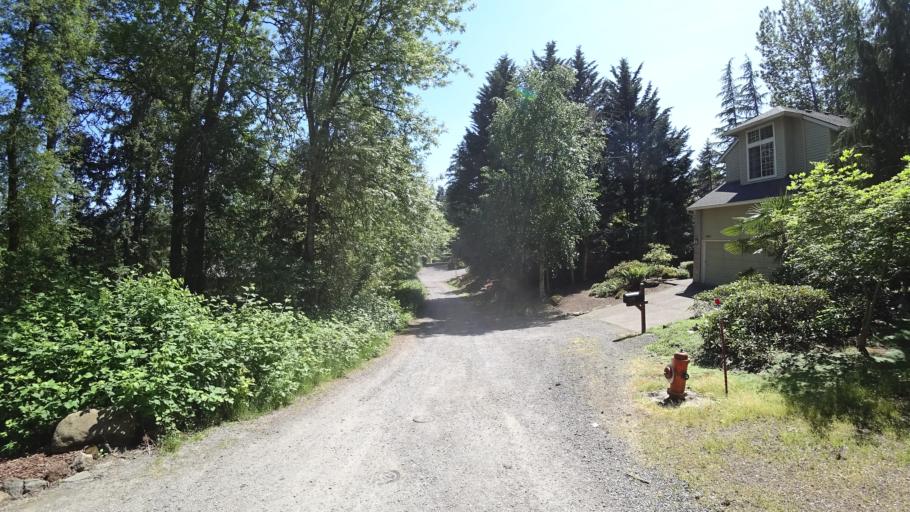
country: US
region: Oregon
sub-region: Washington County
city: Metzger
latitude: 45.4474
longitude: -122.7191
